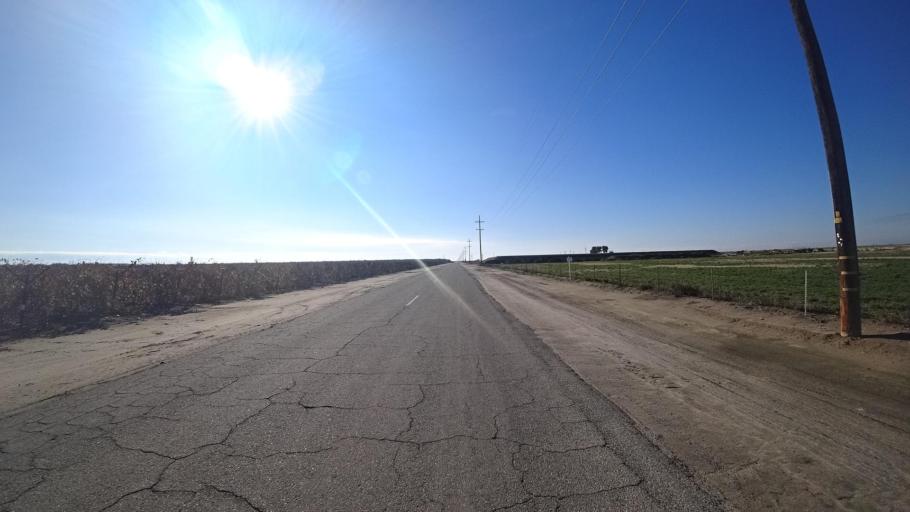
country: US
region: California
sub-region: Kern County
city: McFarland
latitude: 35.6864
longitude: -119.2764
